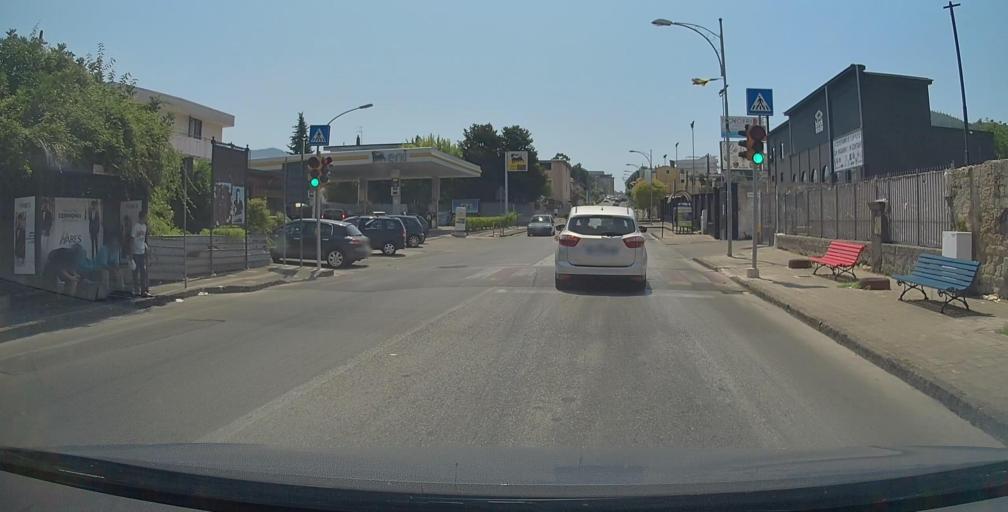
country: IT
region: Campania
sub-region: Provincia di Salerno
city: Nocera Superiore
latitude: 40.7340
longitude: 14.6849
